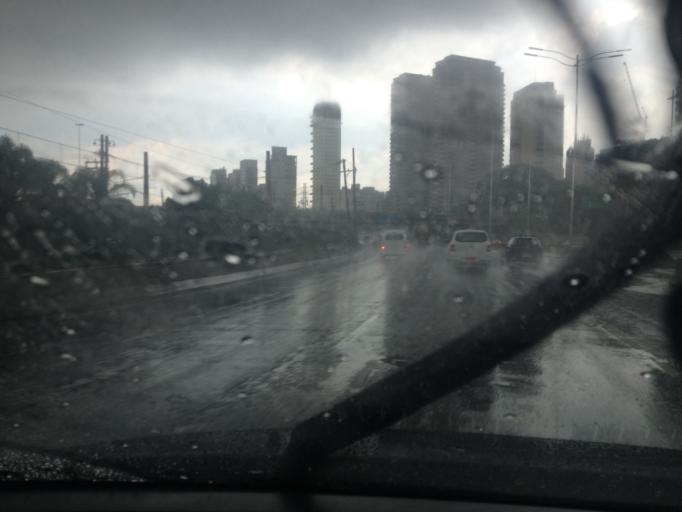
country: BR
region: Sao Paulo
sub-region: Sao Paulo
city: Sao Paulo
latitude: -23.5883
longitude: -46.6908
